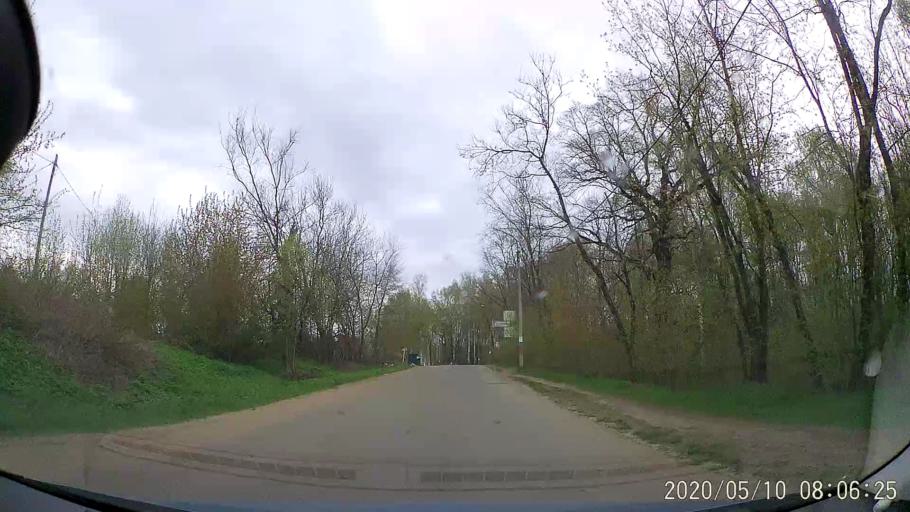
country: RU
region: Jaroslavl
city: Konstantinovskiy
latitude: 57.8243
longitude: 39.5959
